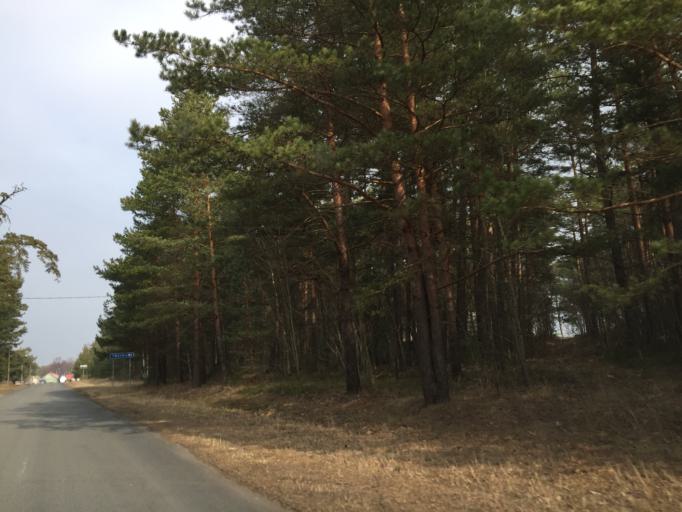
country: LV
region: Salacgrivas
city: Ainazi
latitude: 57.9160
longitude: 24.3860
